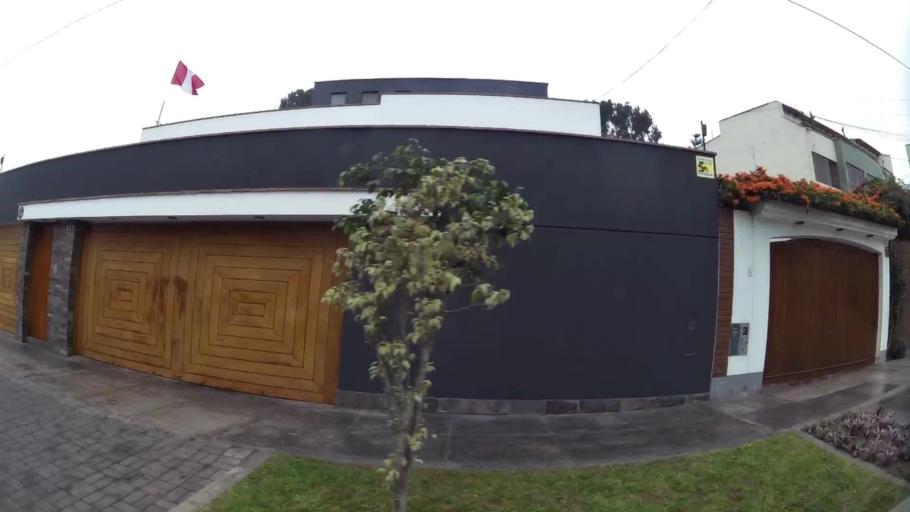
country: PE
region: Lima
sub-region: Lima
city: Surco
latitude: -12.1254
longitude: -76.9919
